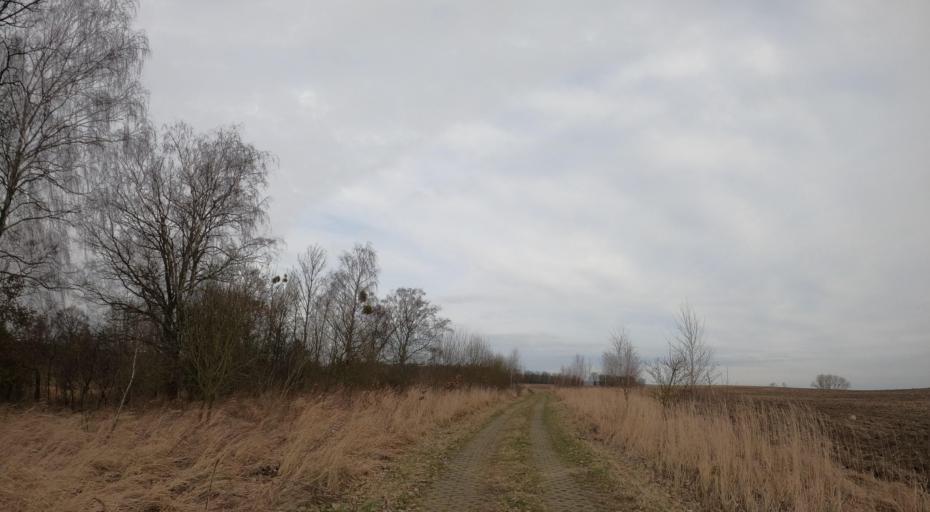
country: PL
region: West Pomeranian Voivodeship
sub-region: Powiat pyrzycki
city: Bielice
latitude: 53.2516
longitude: 14.6395
